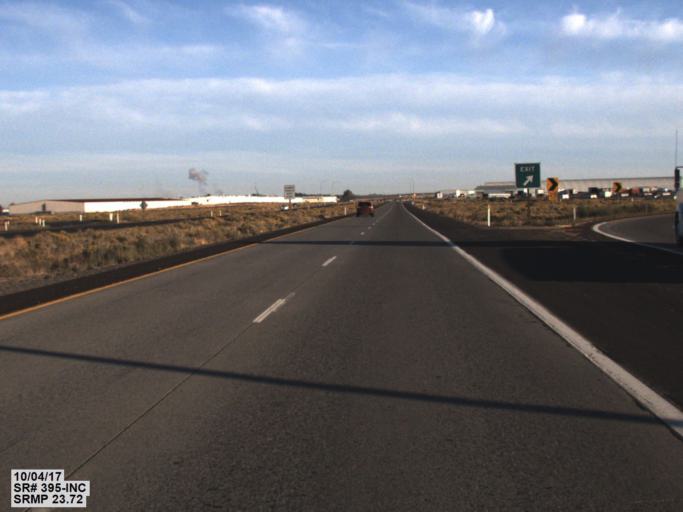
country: US
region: Washington
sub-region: Franklin County
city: Pasco
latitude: 46.2654
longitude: -119.0867
